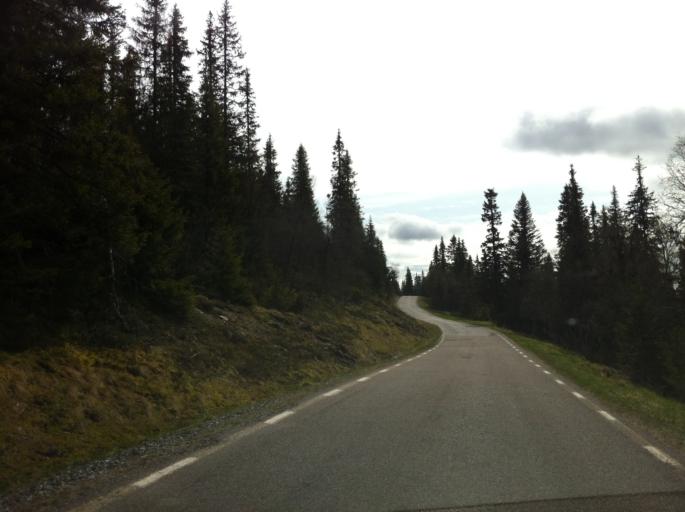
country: NO
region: Hedmark
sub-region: Engerdal
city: Engerdal
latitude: 62.3005
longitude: 12.8025
